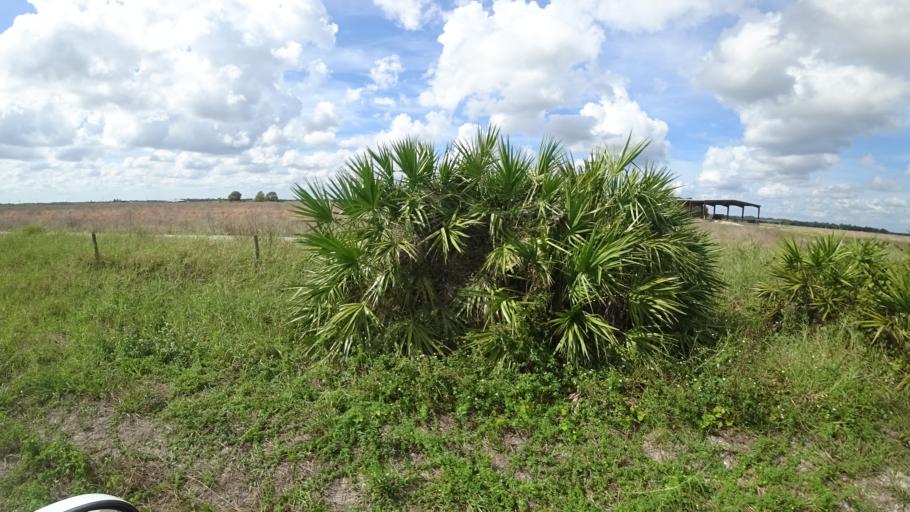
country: US
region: Florida
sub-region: Hillsborough County
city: Wimauma
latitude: 27.5858
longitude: -82.2667
